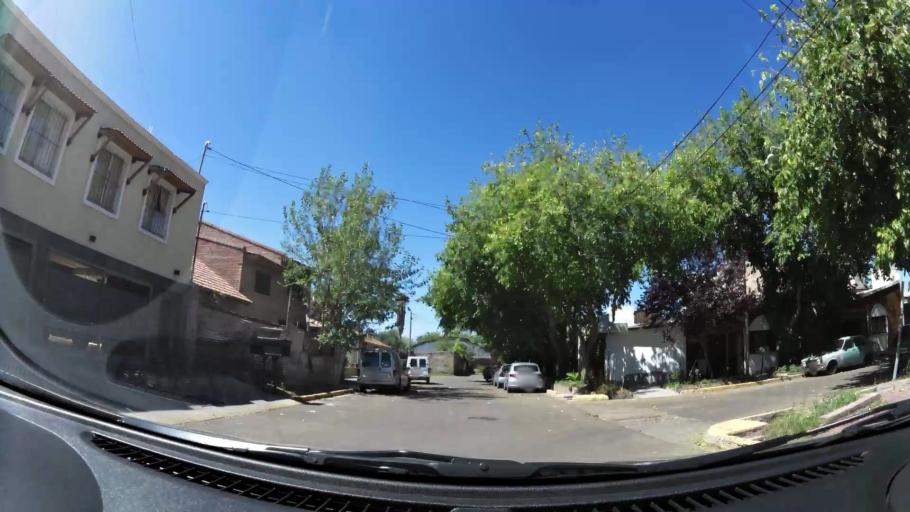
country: AR
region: Mendoza
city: Las Heras
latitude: -32.8536
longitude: -68.8482
